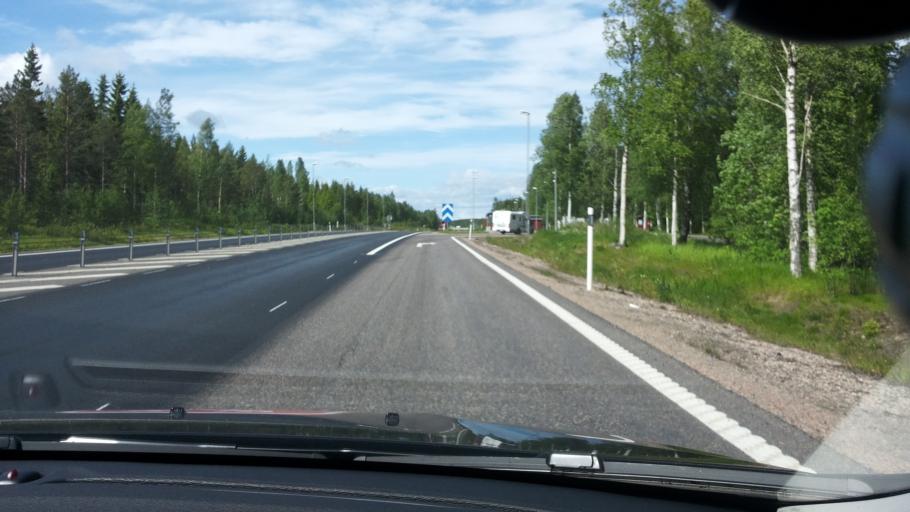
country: SE
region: Vaesternorrland
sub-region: Sundsvalls Kommun
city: Njurundabommen
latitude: 62.1669
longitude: 17.3556
